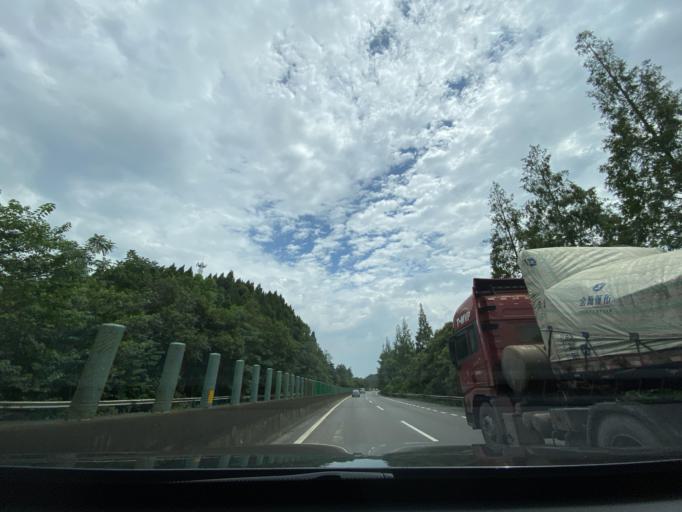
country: CN
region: Sichuan
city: Jiancheng
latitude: 30.3125
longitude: 104.5774
